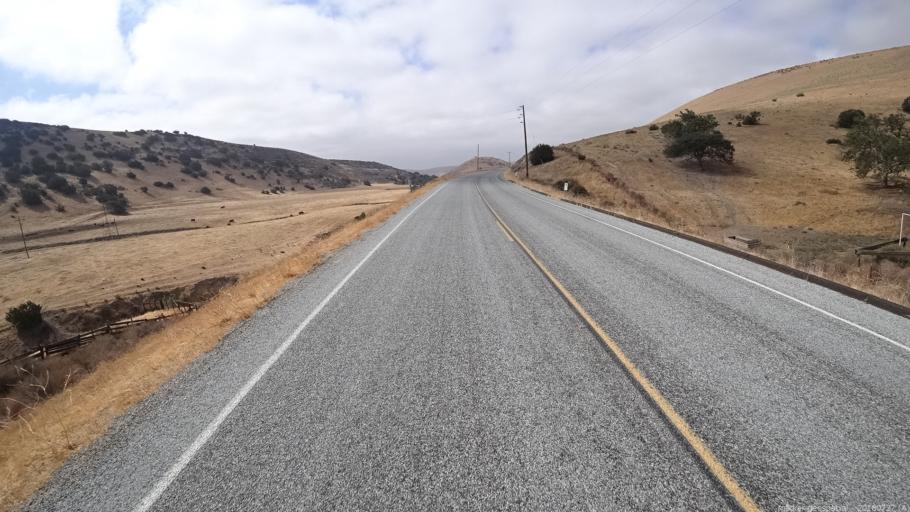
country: US
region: California
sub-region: Monterey County
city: King City
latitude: 36.2861
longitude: -121.0561
